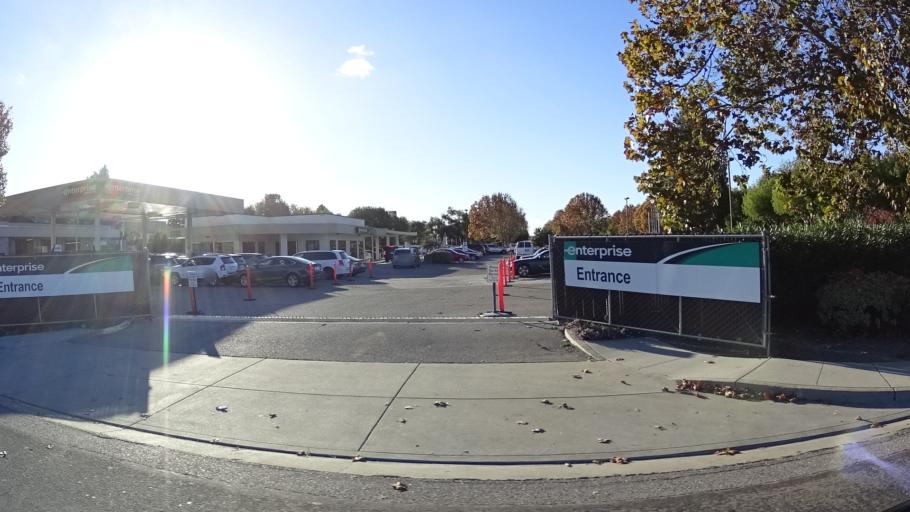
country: US
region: California
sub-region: Santa Clara County
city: Santa Clara
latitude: 37.3695
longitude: -121.9416
